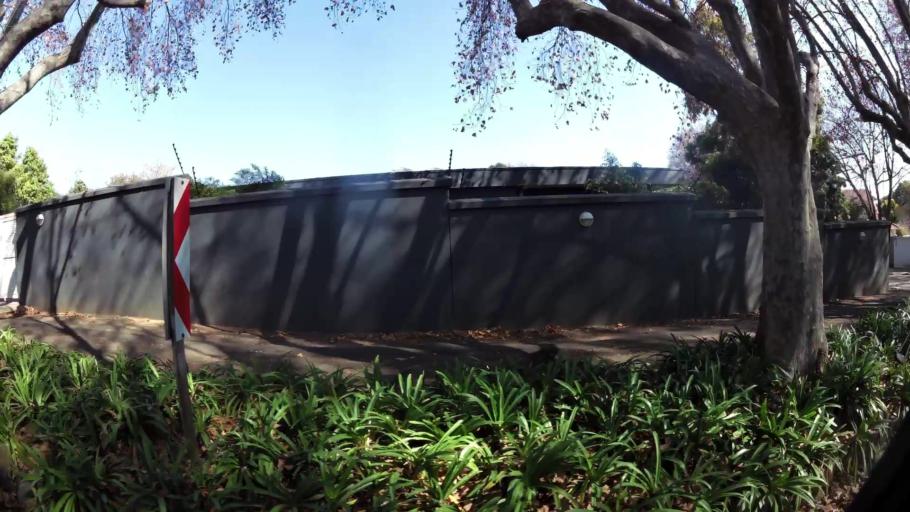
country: ZA
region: Gauteng
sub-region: City of Johannesburg Metropolitan Municipality
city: Johannesburg
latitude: -26.1715
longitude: 28.0380
